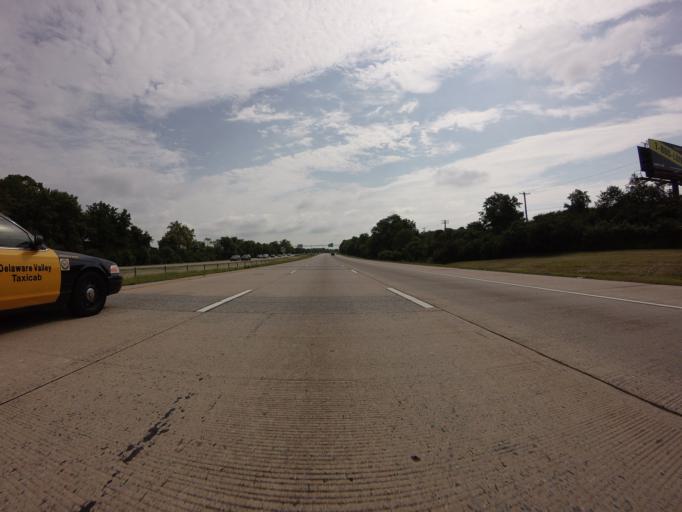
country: US
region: Delaware
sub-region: New Castle County
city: Wilmington Manor
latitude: 39.7158
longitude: -75.5727
